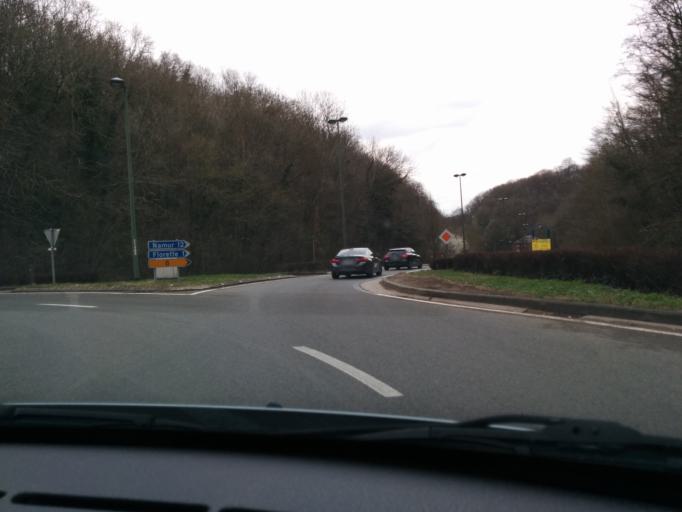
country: BE
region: Wallonia
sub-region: Province de Namur
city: Floreffe
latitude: 50.4253
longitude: 4.7528
